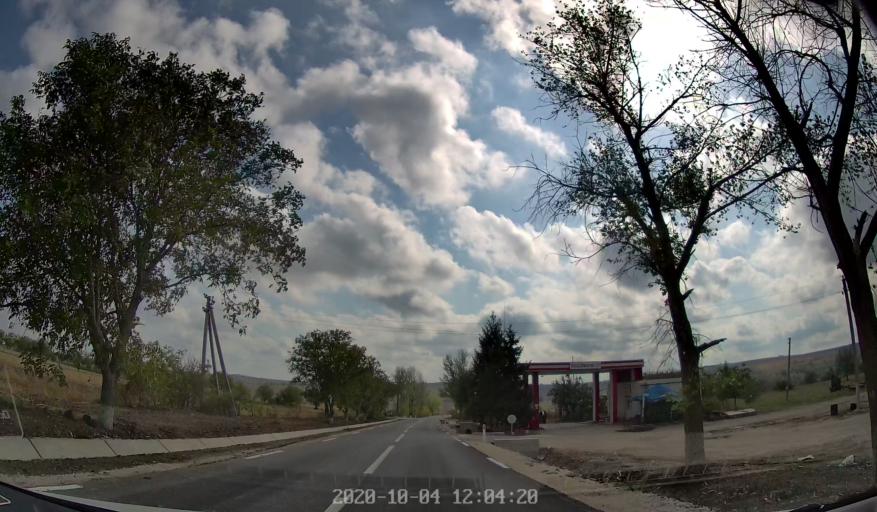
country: MD
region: Rezina
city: Saharna
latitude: 47.6047
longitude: 28.9415
